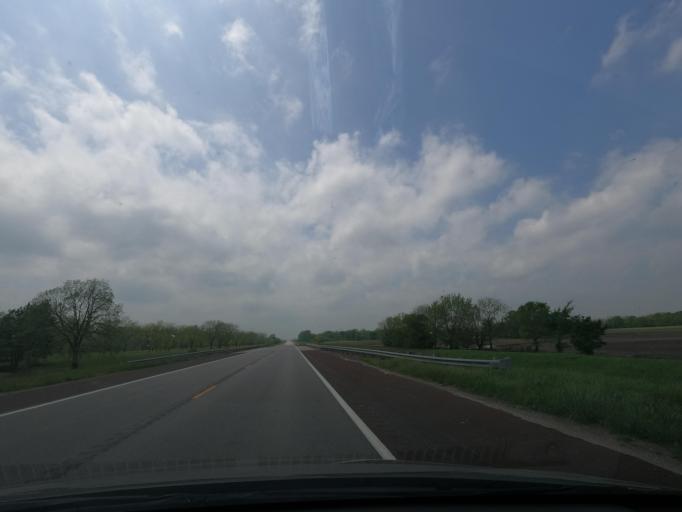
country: US
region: Kansas
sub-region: Labette County
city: Parsons
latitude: 37.3401
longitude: -95.0978
